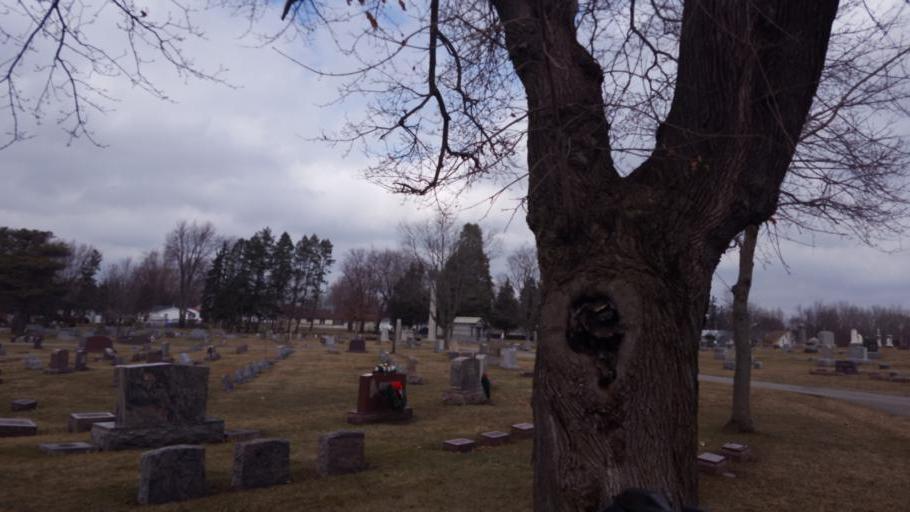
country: US
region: Ohio
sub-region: Richland County
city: Shelby
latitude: 40.8718
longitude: -82.6654
